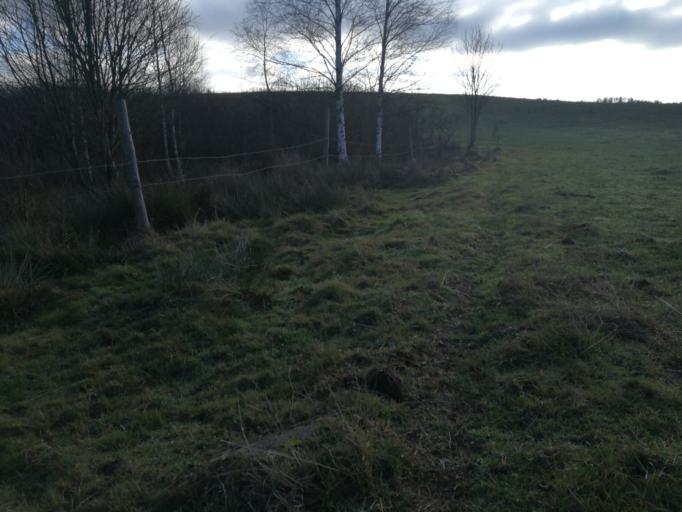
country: PL
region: Warmian-Masurian Voivodeship
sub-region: Powiat dzialdowski
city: Rybno
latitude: 53.4131
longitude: 19.9138
